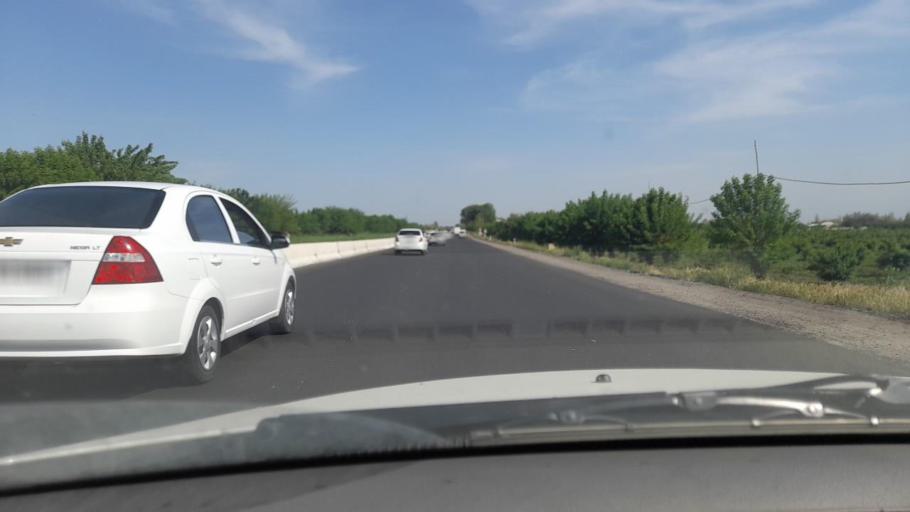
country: UZ
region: Samarqand
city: Chelak
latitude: 39.8446
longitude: 66.8115
